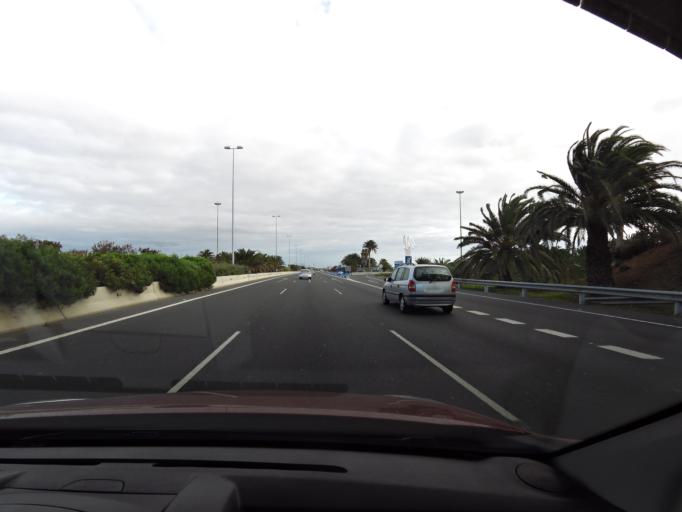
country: ES
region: Canary Islands
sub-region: Provincia de Las Palmas
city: Cruce de Arinaga
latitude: 27.8404
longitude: -15.4394
